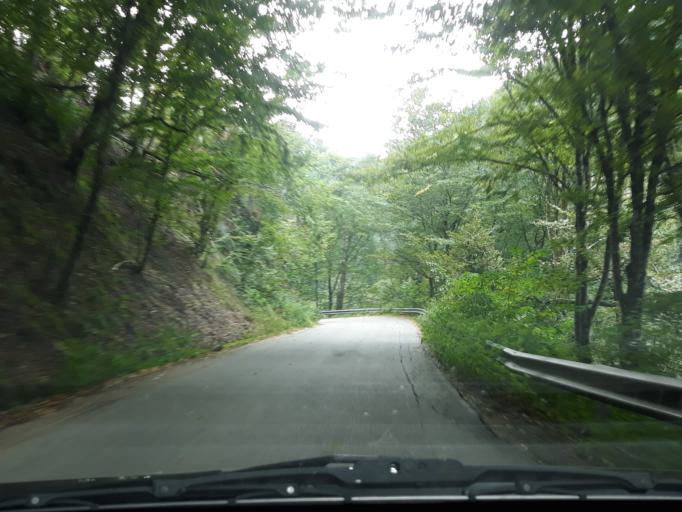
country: RO
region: Bihor
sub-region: Comuna Pietroasa
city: Pietroasa
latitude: 46.5966
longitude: 22.6369
